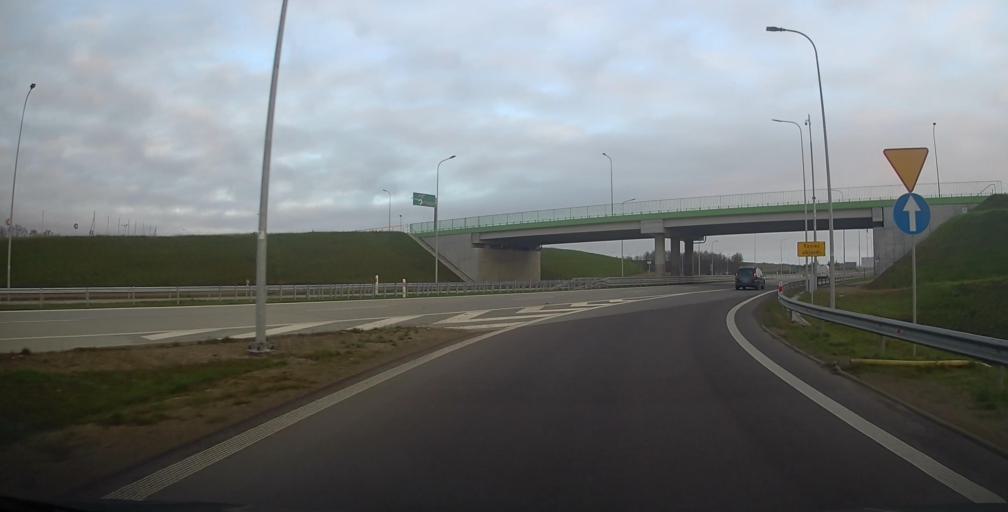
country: PL
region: Podlasie
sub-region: Powiat lomzynski
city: Piatnica
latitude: 53.2493
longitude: 22.1055
